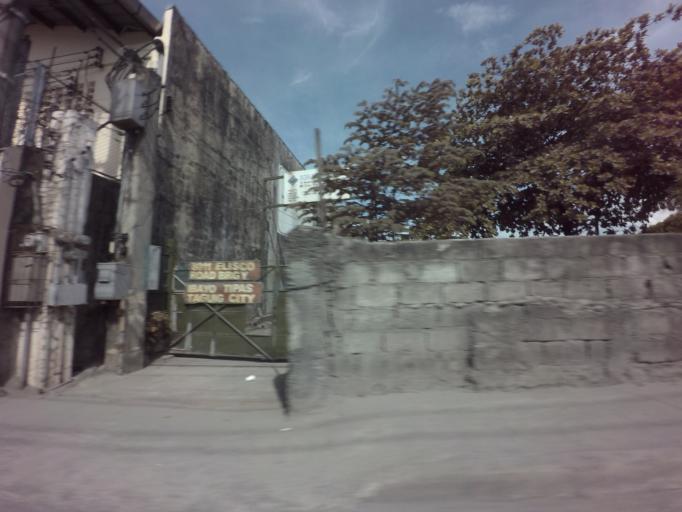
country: PH
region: Calabarzon
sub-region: Province of Rizal
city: Pateros
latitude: 14.5430
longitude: 121.0886
